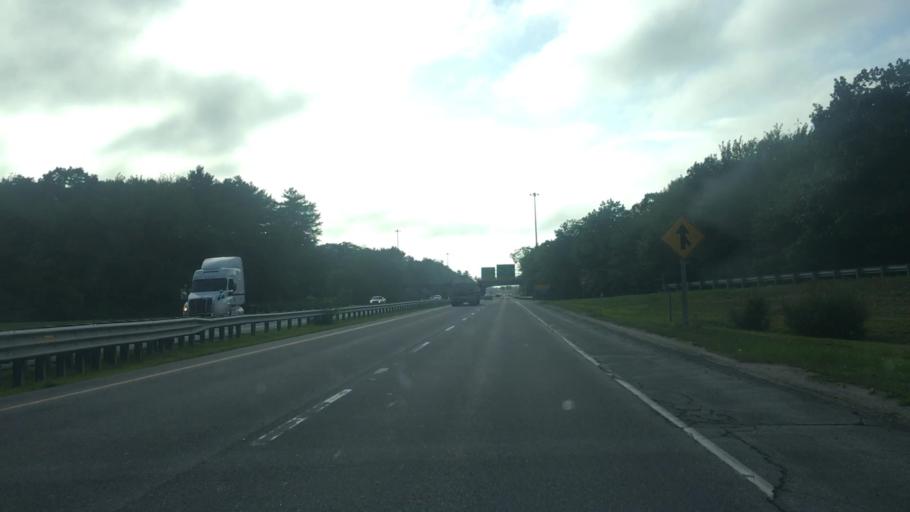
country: US
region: Maine
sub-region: Cumberland County
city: South Portland Gardens
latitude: 43.6257
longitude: -70.3251
